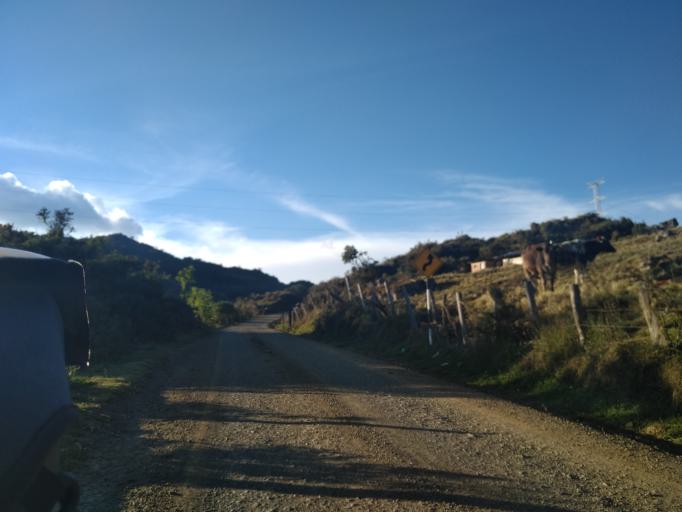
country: PE
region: Amazonas
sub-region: Provincia de Chachapoyas
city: Montevideo
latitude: -6.7163
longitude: -77.8658
